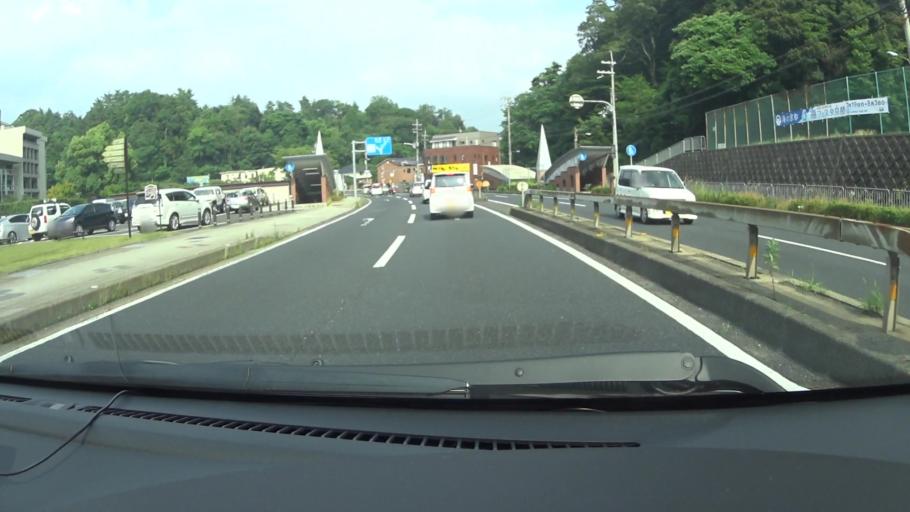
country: JP
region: Kyoto
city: Maizuru
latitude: 35.4742
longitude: 135.3847
